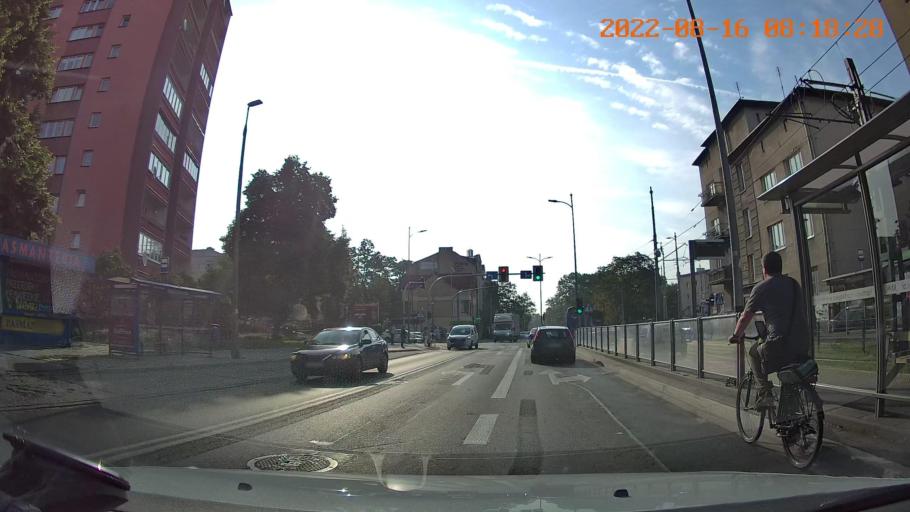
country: PL
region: Lesser Poland Voivodeship
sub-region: Krakow
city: Krakow
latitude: 50.0779
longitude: 19.9006
